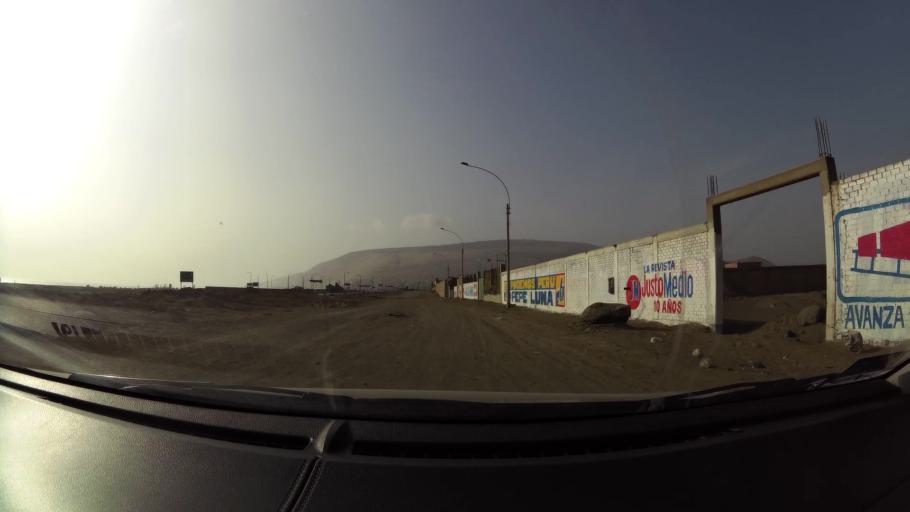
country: PE
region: Lima
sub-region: Lima
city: Santa Rosa
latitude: -11.7585
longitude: -77.1620
